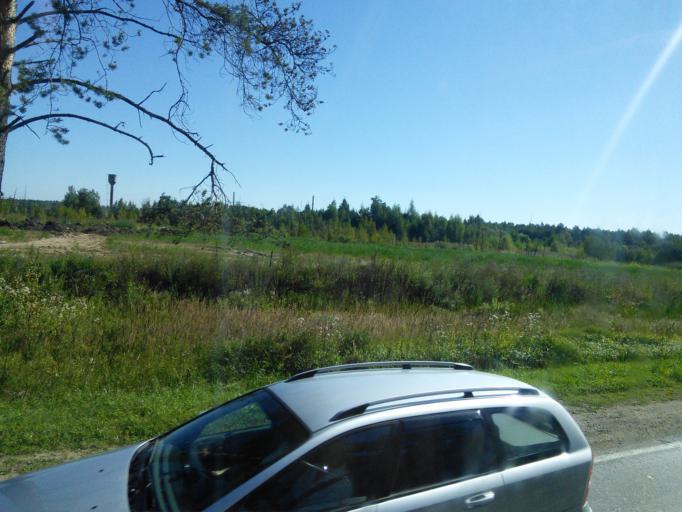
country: RU
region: Jaroslavl
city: Uglich
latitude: 57.4884
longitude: 38.3556
